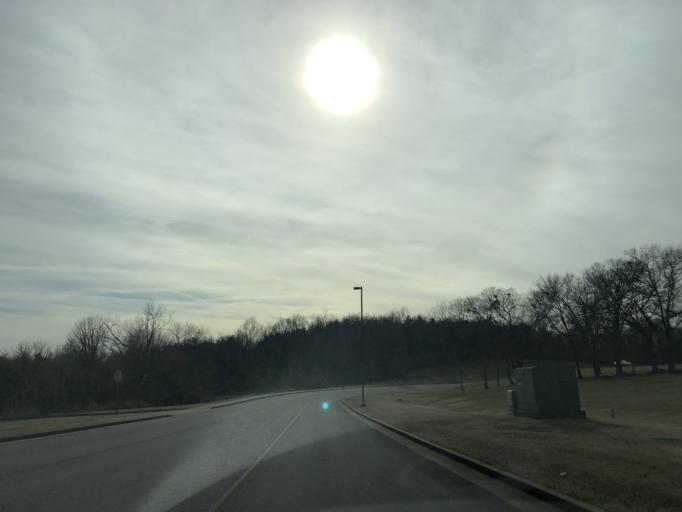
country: US
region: Tennessee
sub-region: Davidson County
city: Nashville
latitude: 36.2139
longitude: -86.7398
